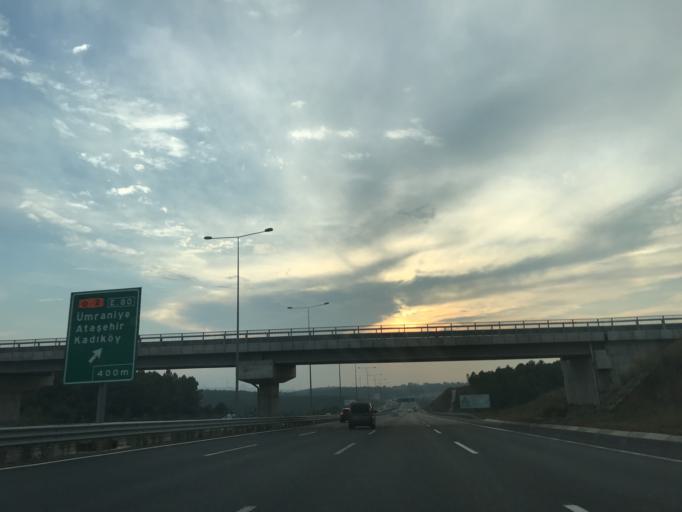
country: TR
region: Istanbul
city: Umraniye
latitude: 41.0495
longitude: 29.1451
